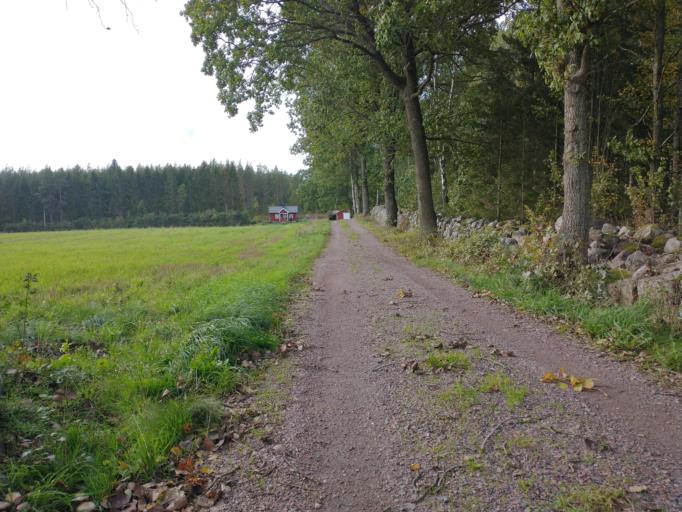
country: SE
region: Kalmar
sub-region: Kalmar Kommun
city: Lindsdal
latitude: 56.7735
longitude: 16.3024
